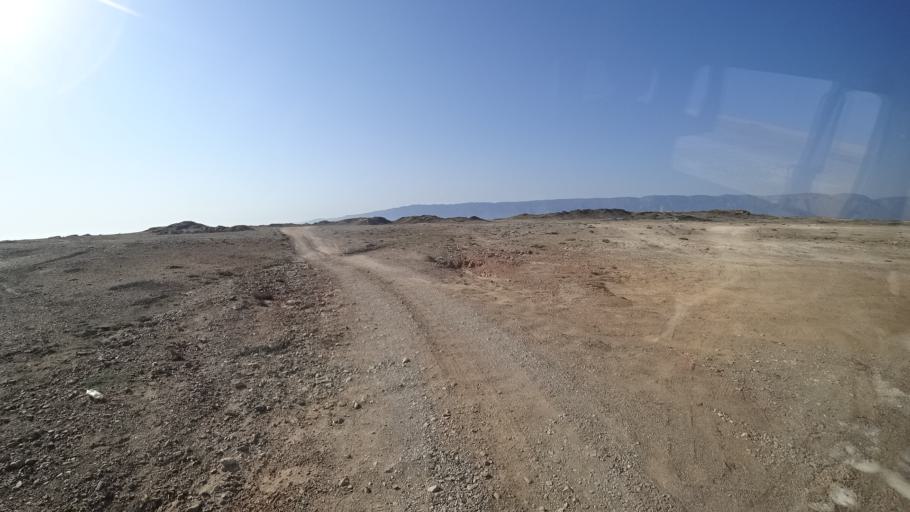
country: OM
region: Zufar
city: Salalah
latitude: 16.9465
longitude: 54.7992
